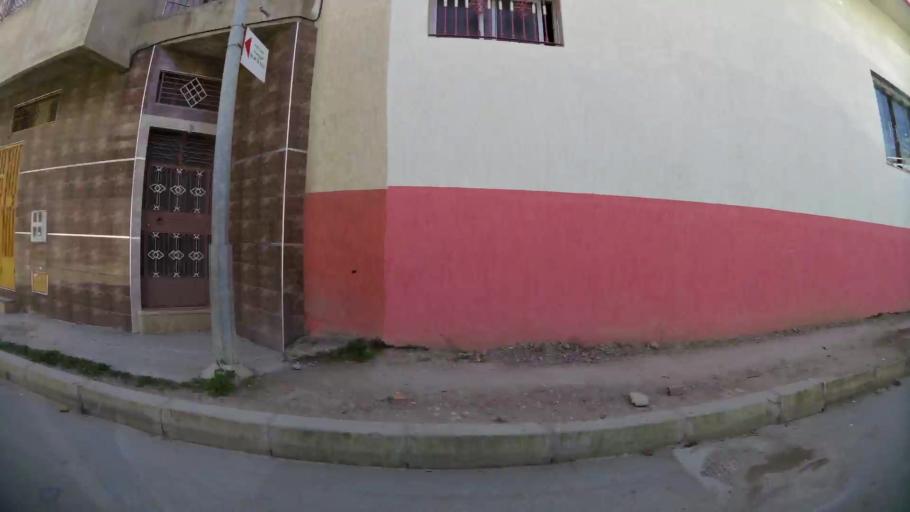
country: MA
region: Tanger-Tetouan
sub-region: Tanger-Assilah
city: Tangier
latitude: 35.7328
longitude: -5.8091
